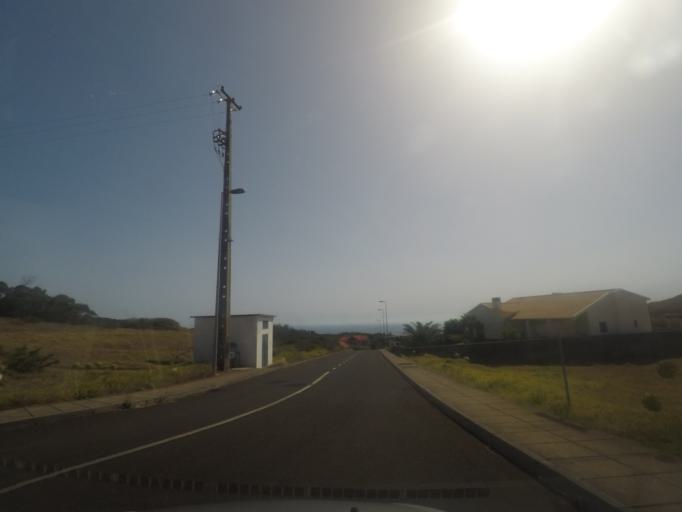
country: PT
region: Madeira
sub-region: Calheta
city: Faja da Ovelha
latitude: 32.8156
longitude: -17.2541
